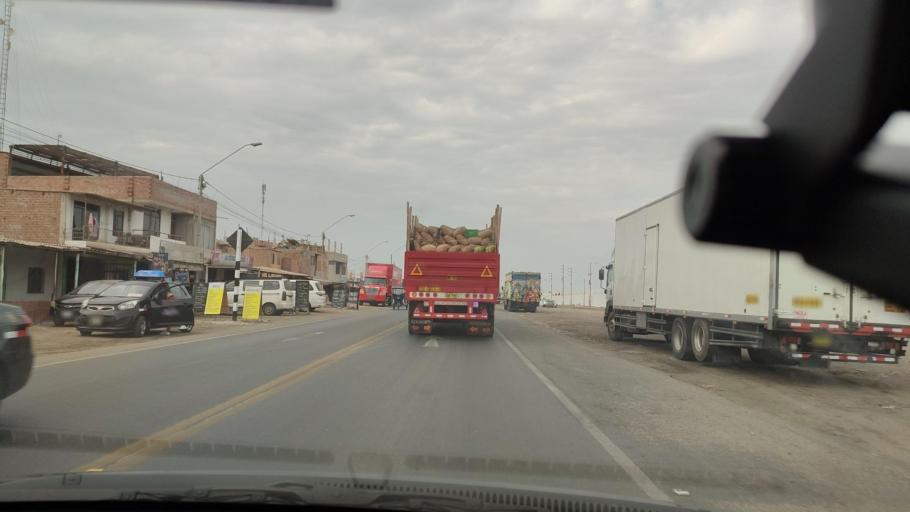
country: PE
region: La Libertad
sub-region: Provincia de Trujillo
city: Huanchaco
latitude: -8.0884
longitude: -79.0967
